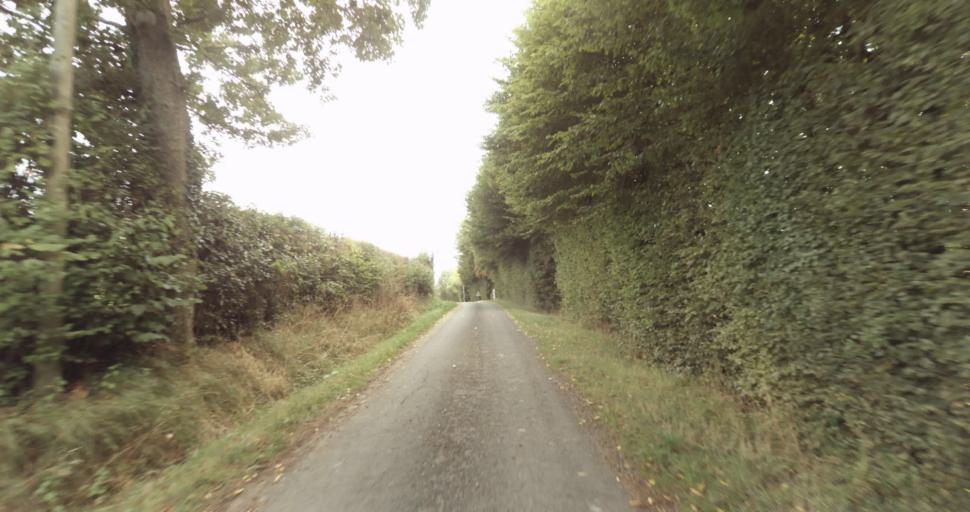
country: FR
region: Lower Normandy
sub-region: Departement de l'Orne
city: Gace
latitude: 48.8443
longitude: 0.2251
